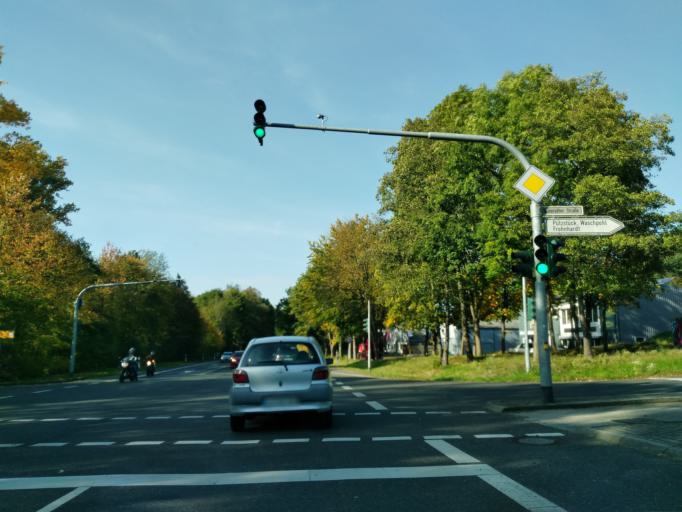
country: DE
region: North Rhine-Westphalia
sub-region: Regierungsbezirk Koln
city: Hennef
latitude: 50.7109
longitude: 7.2823
